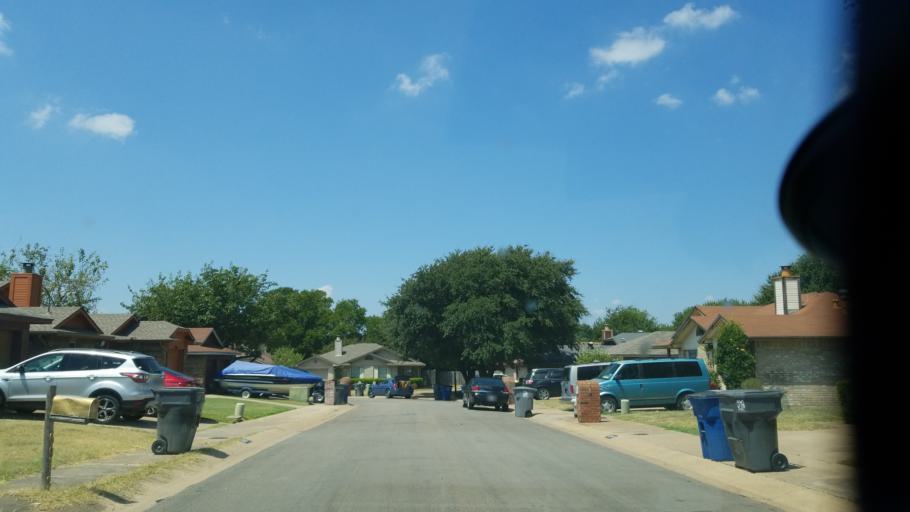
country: US
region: Texas
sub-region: Dallas County
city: Duncanville
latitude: 32.6649
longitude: -96.8861
